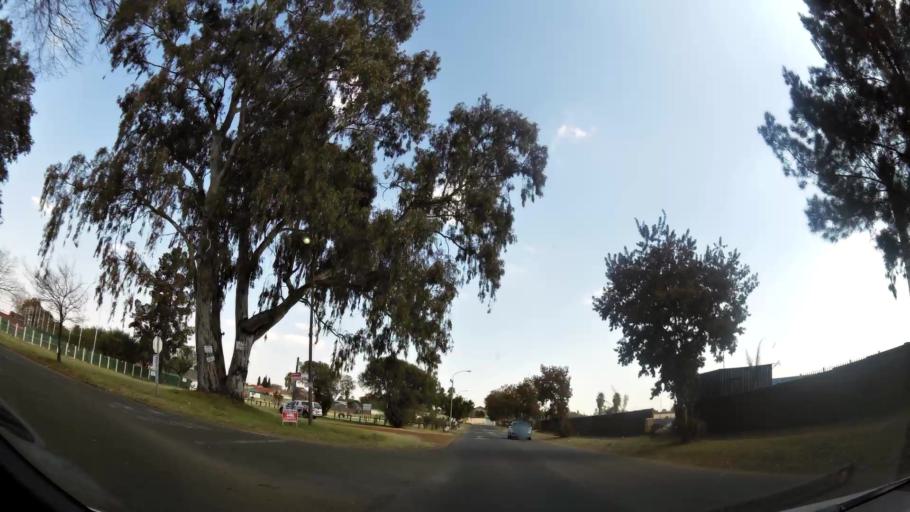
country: ZA
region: Gauteng
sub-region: Ekurhuleni Metropolitan Municipality
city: Boksburg
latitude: -26.1890
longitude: 28.2302
